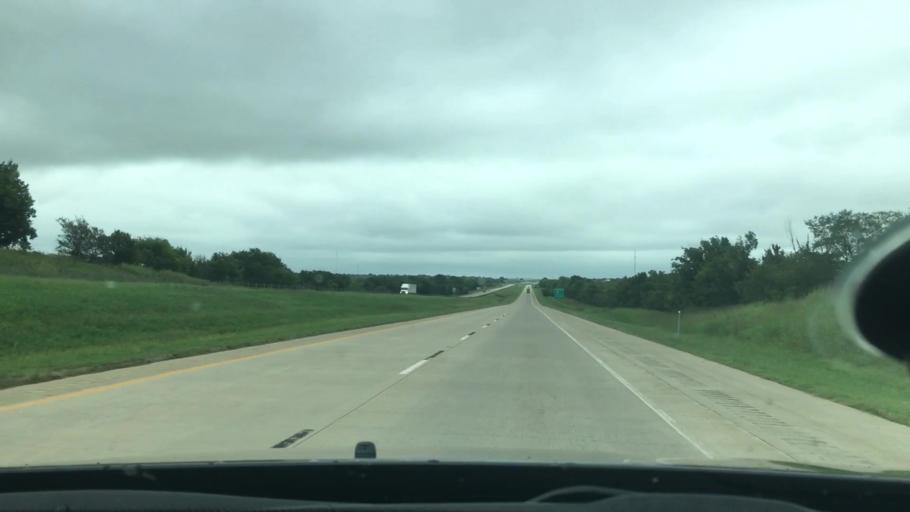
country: US
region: Oklahoma
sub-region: McIntosh County
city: Checotah
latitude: 35.4571
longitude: -95.5740
